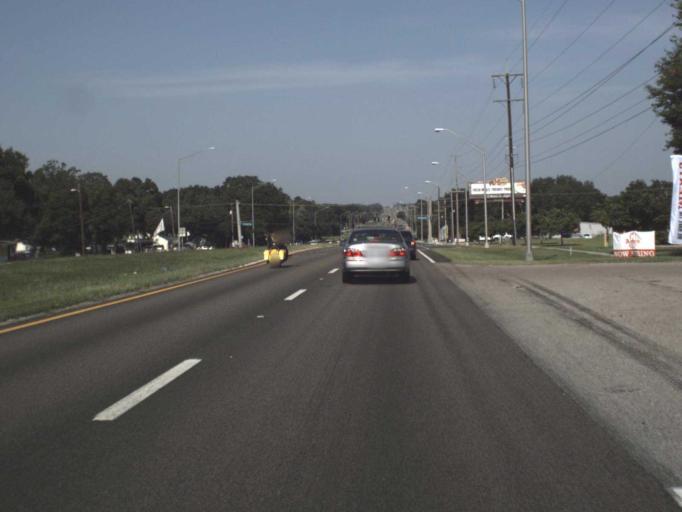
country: US
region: Florida
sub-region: Hillsborough County
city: Valrico
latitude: 27.9379
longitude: -82.2257
